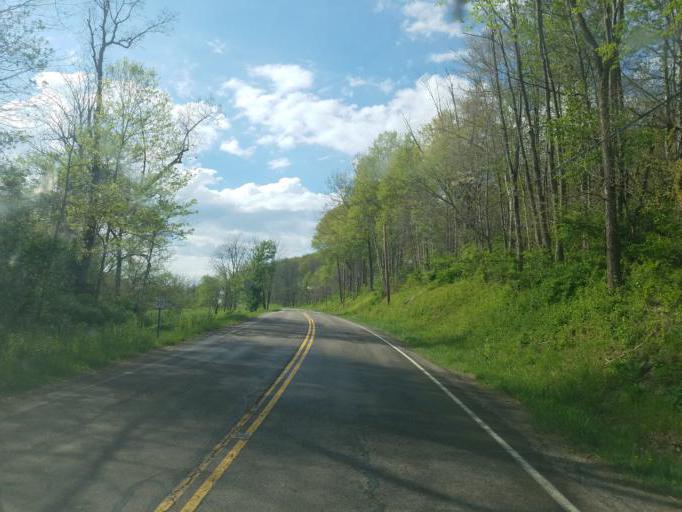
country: US
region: Ohio
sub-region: Knox County
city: Oak Hill
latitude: 40.3955
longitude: -82.2704
